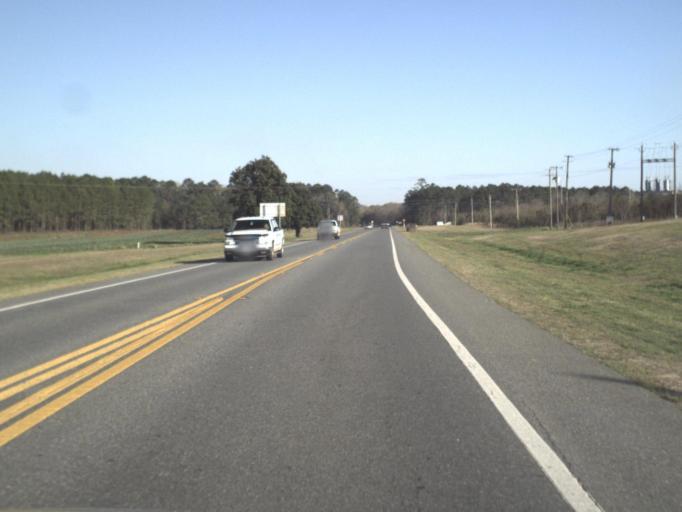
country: US
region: Florida
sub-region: Gadsden County
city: Chattahoochee
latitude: 30.7013
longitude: -84.8793
